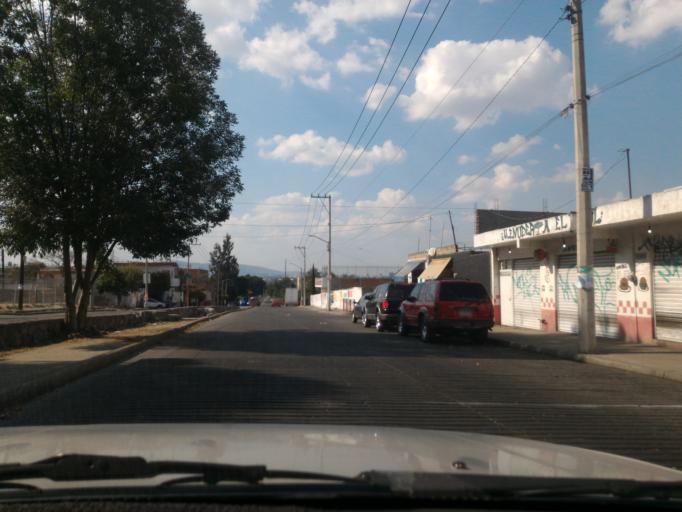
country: MX
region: Jalisco
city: Guadalajara
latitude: 20.6222
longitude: -103.3805
